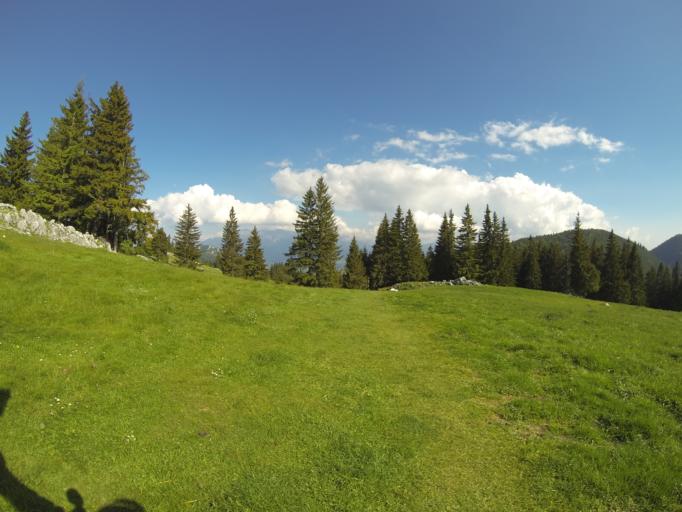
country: RO
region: Brasov
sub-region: Comuna Zarnesti
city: Zarnesti
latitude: 45.5400
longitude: 25.2749
